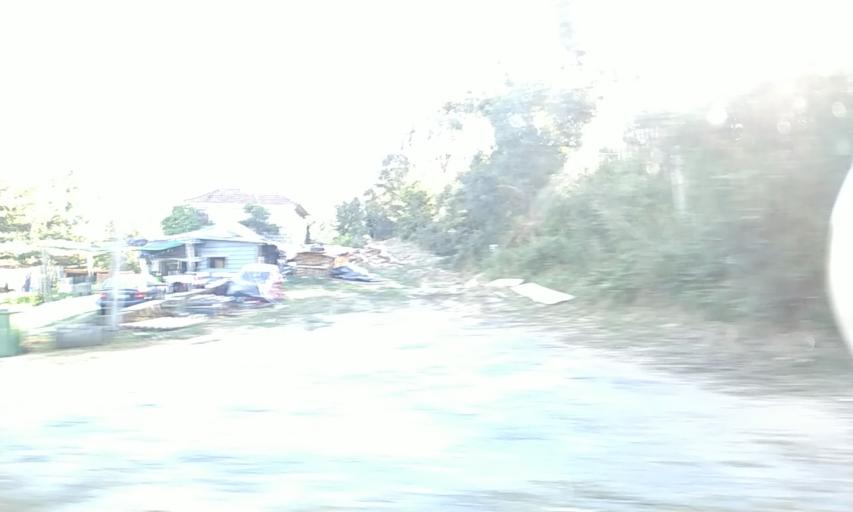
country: PT
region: Porto
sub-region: Pacos de Ferreira
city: Seroa
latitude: 41.2784
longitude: -8.4698
